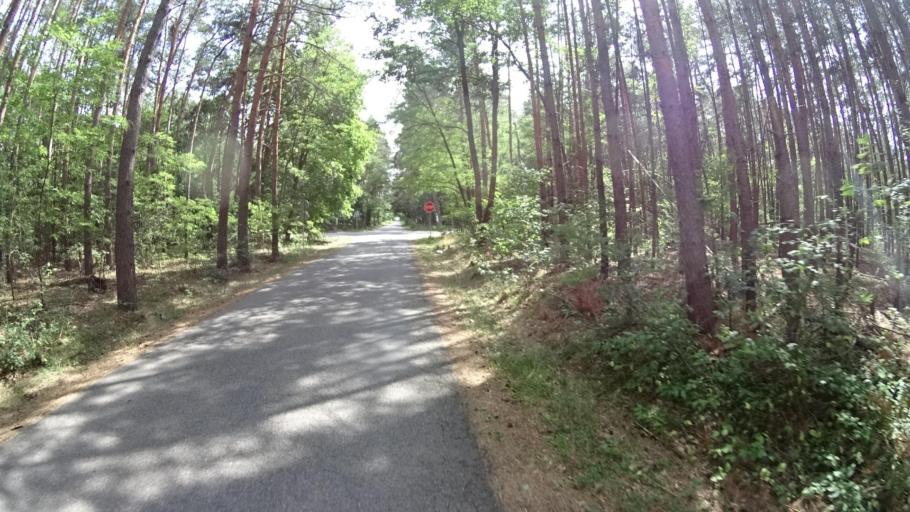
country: PL
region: Masovian Voivodeship
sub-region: Powiat bialobrzeski
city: Wysmierzyce
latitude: 51.6278
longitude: 20.8556
